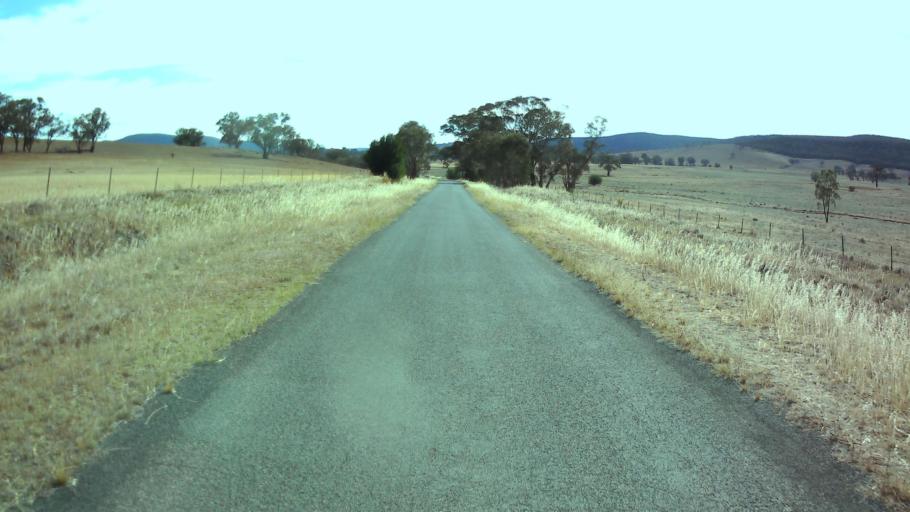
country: AU
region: New South Wales
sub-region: Weddin
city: Grenfell
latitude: -33.8272
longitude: 148.2848
